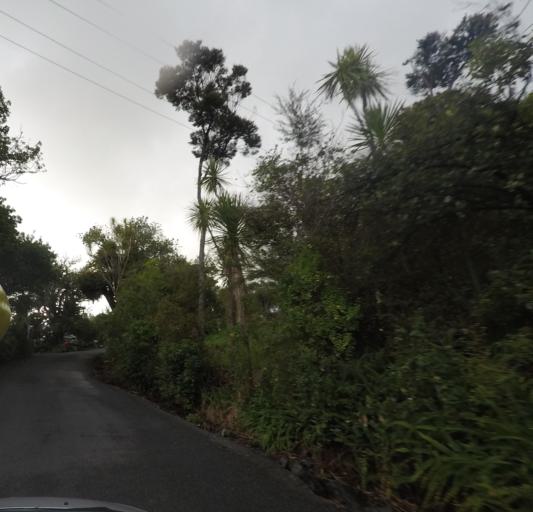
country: NZ
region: Auckland
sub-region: Auckland
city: Warkworth
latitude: -36.3811
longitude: 174.7581
